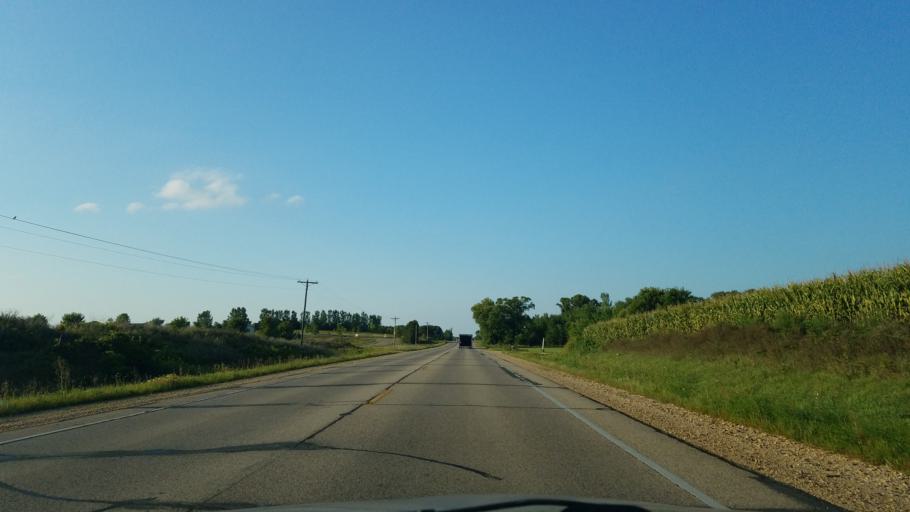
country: US
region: Wisconsin
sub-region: Saint Croix County
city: New Richmond
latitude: 45.0697
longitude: -92.5374
